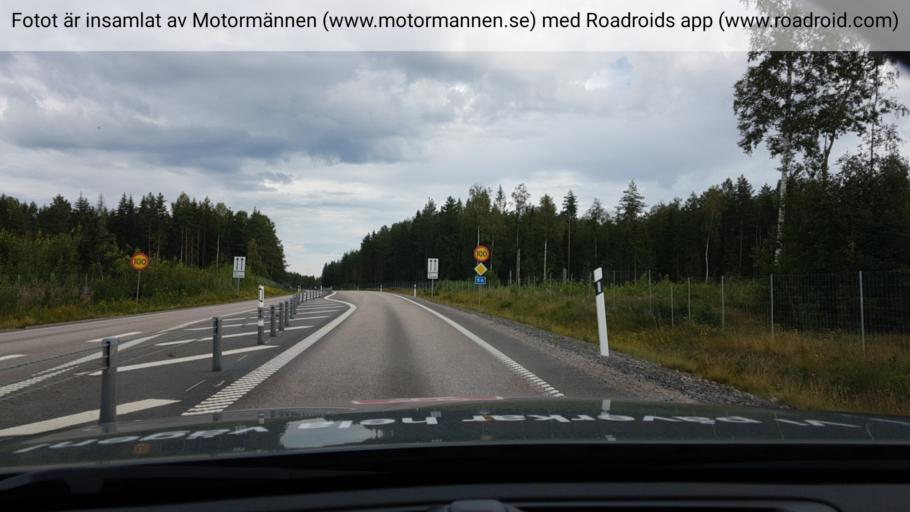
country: SE
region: Uppsala
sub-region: Heby Kommun
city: Heby
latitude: 59.9581
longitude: 16.8390
